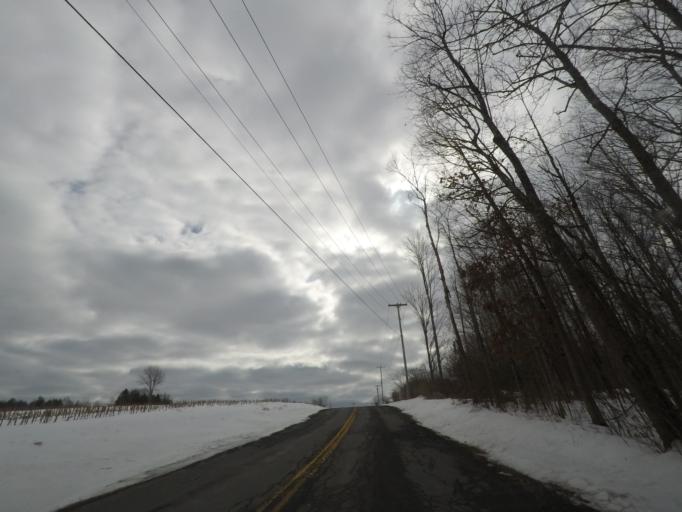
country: US
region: New York
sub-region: Rensselaer County
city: Hoosick Falls
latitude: 42.9408
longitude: -73.4321
